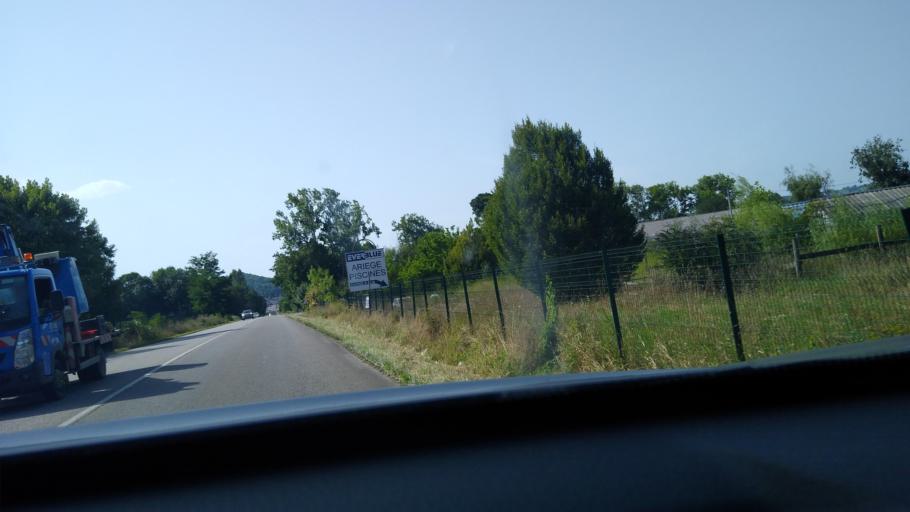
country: FR
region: Midi-Pyrenees
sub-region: Departement de l'Ariege
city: Saint-Lizier
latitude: 43.0228
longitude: 1.0958
